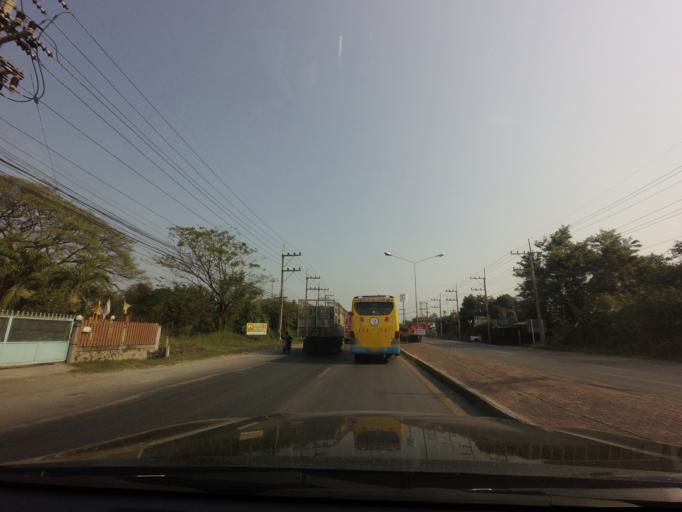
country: TH
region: Kanchanaburi
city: Tha Maka
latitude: 13.8849
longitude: 99.8019
